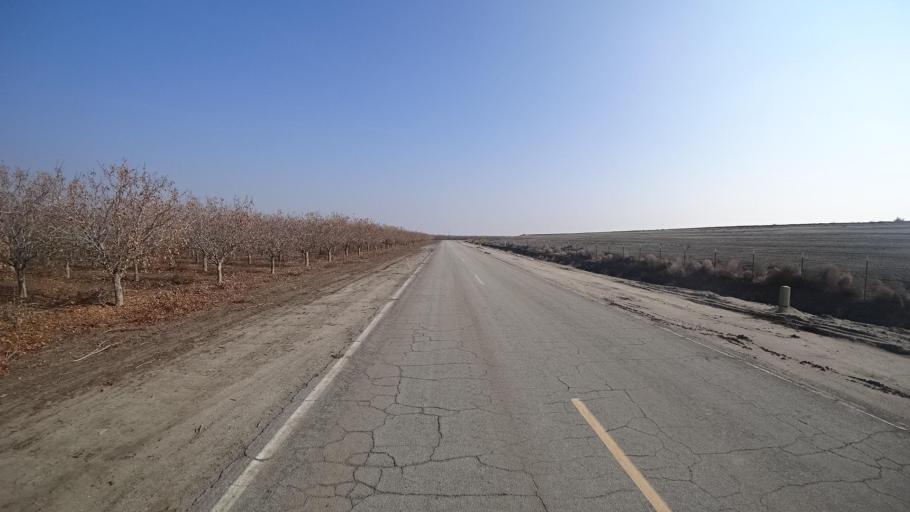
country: US
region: California
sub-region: Kern County
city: Buttonwillow
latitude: 35.3403
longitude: -119.3801
